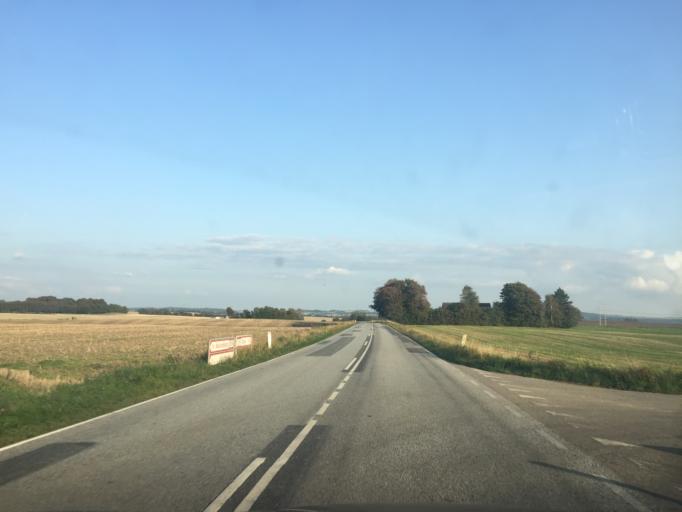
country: DK
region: Zealand
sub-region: Kalundborg Kommune
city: Svebolle
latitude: 55.6079
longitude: 11.2567
